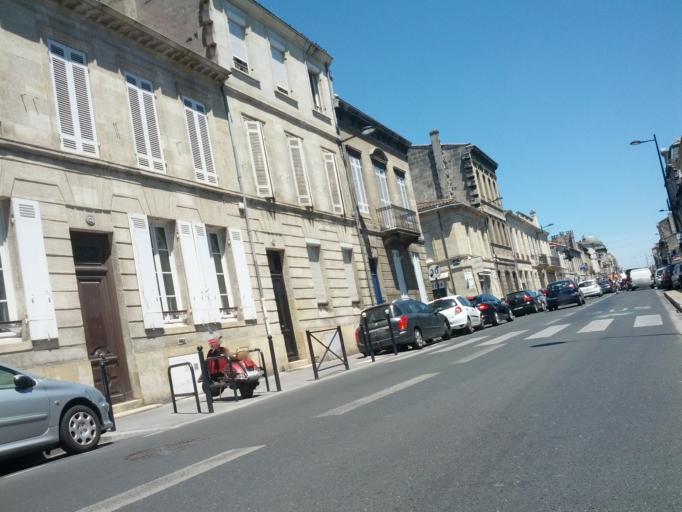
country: FR
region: Aquitaine
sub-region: Departement de la Gironde
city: Bordeaux
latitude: 44.8571
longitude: -0.5687
